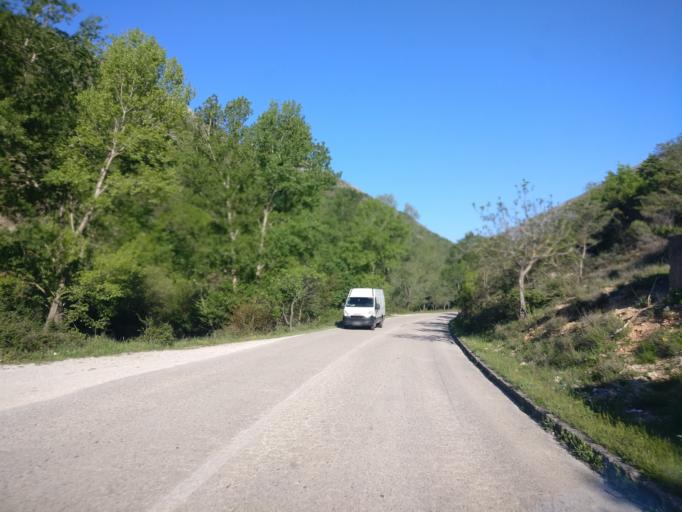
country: BA
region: Federation of Bosnia and Herzegovina
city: Stolac
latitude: 43.0871
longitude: 18.0023
